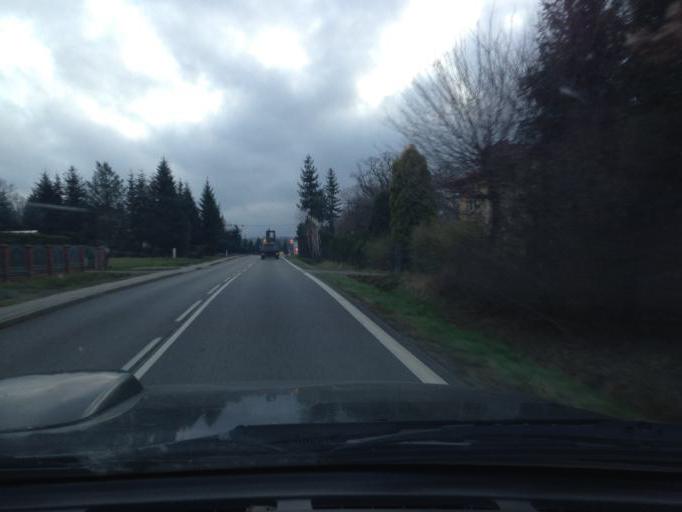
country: PL
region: Subcarpathian Voivodeship
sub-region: Powiat jasielski
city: Nowy Zmigrod
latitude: 49.6108
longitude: 21.5307
